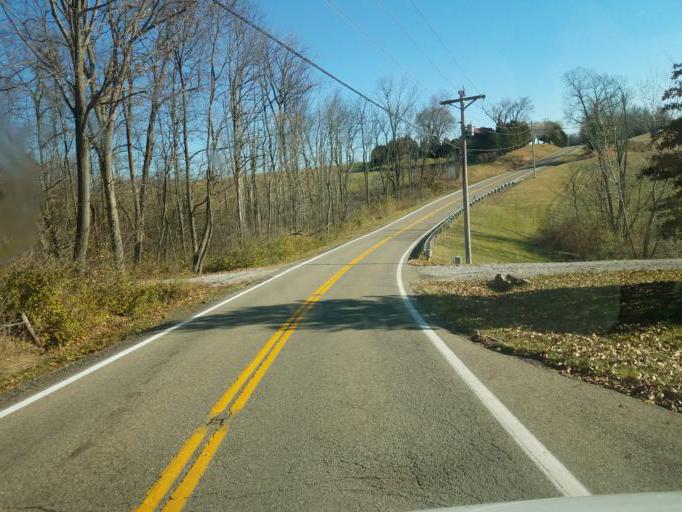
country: US
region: Ohio
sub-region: Muskingum County
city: Dresden
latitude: 40.2550
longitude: -82.0609
